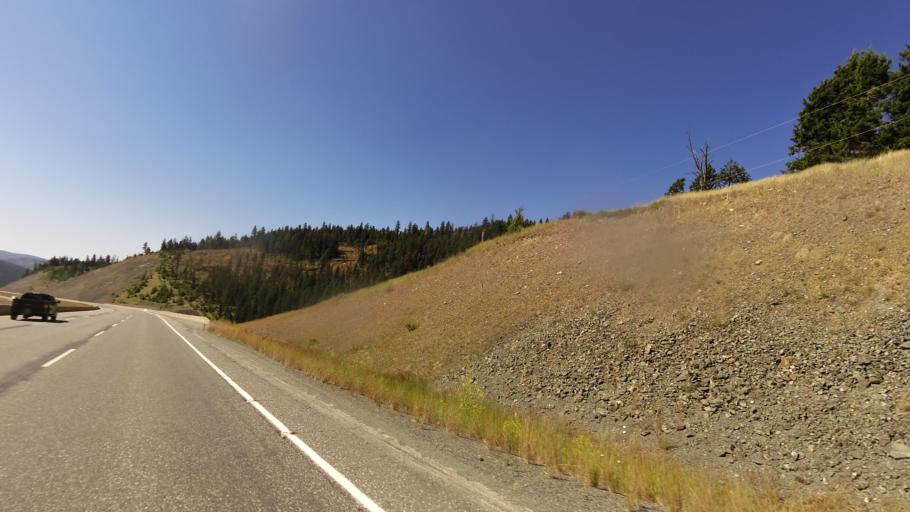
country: CA
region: British Columbia
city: Merritt
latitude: 50.2460
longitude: -120.6305
